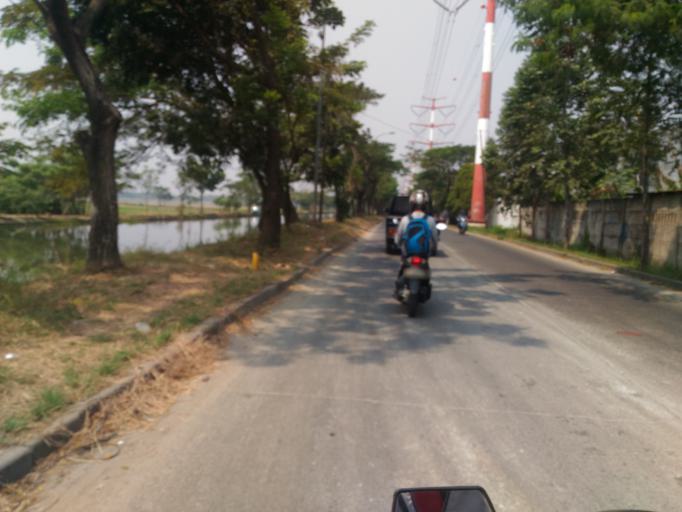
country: ID
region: Banten
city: Tangerang
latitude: -6.1503
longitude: 106.6021
